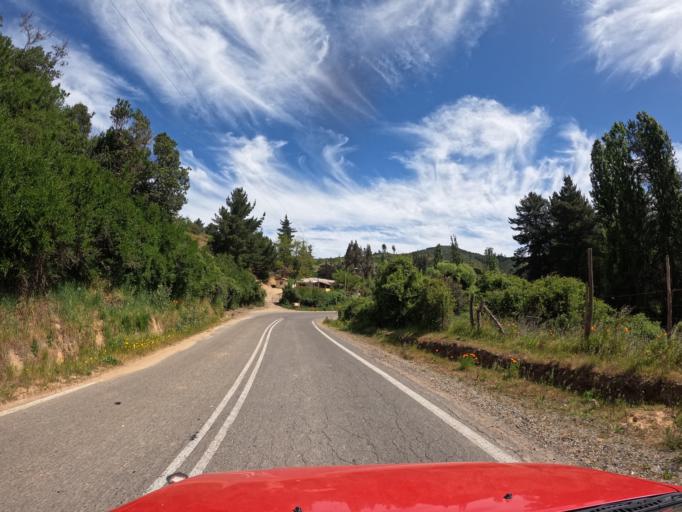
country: CL
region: Maule
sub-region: Provincia de Talca
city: Talca
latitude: -35.0095
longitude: -71.9713
